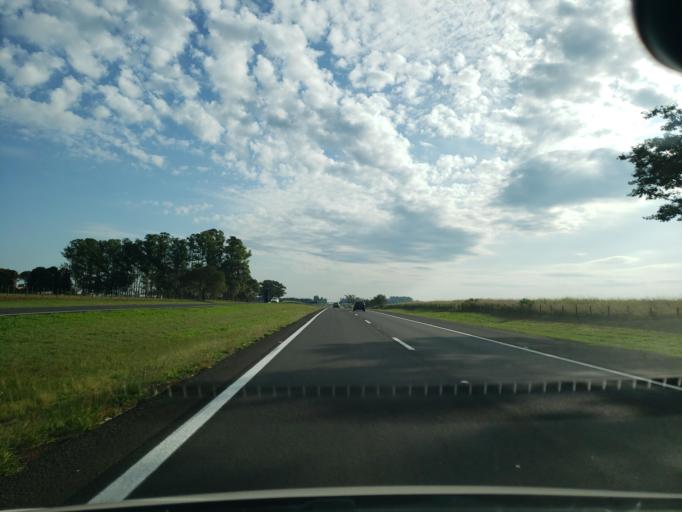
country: BR
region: Sao Paulo
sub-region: Guararapes
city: Guararapes
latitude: -21.2019
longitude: -50.5927
